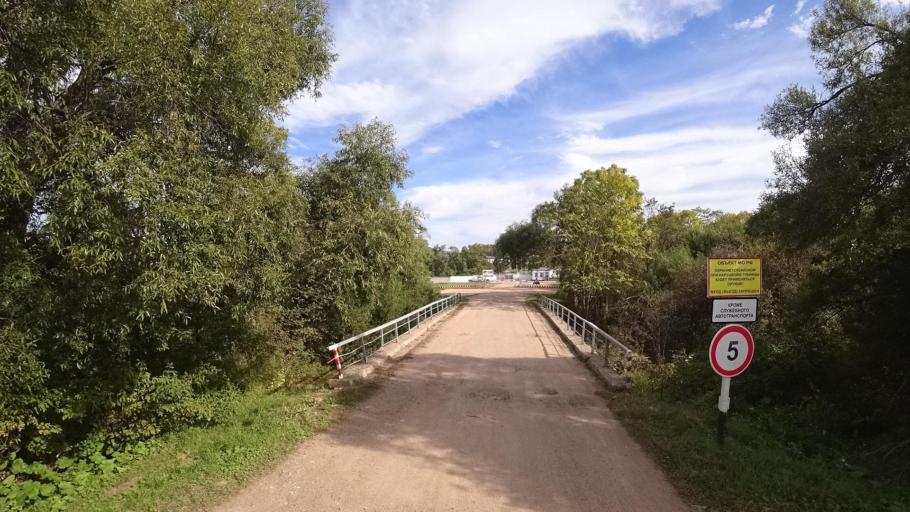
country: RU
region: Primorskiy
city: Dostoyevka
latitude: 44.2966
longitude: 133.4632
